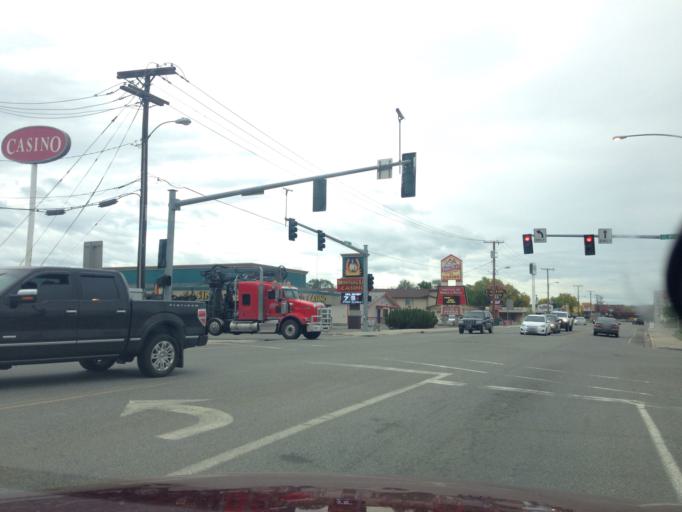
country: US
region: Montana
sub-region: Yellowstone County
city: Laurel
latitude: 45.6651
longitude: -108.7714
